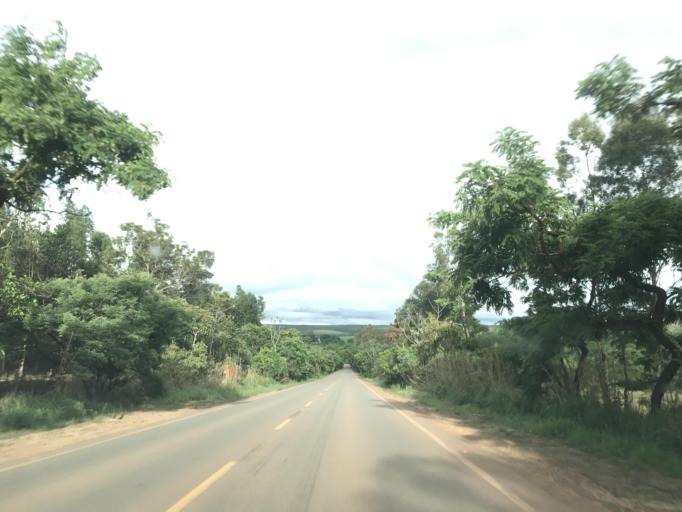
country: BR
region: Goias
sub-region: Vianopolis
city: Vianopolis
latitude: -16.5783
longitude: -48.3385
